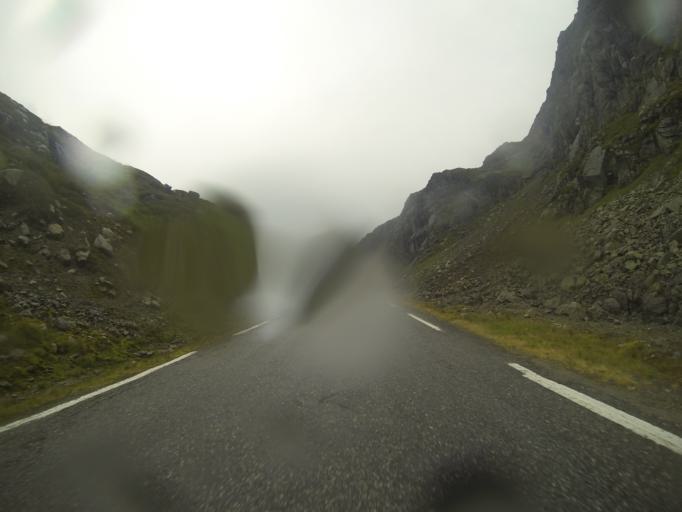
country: NO
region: Hordaland
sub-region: Odda
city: Odda
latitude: 59.7700
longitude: 6.7402
